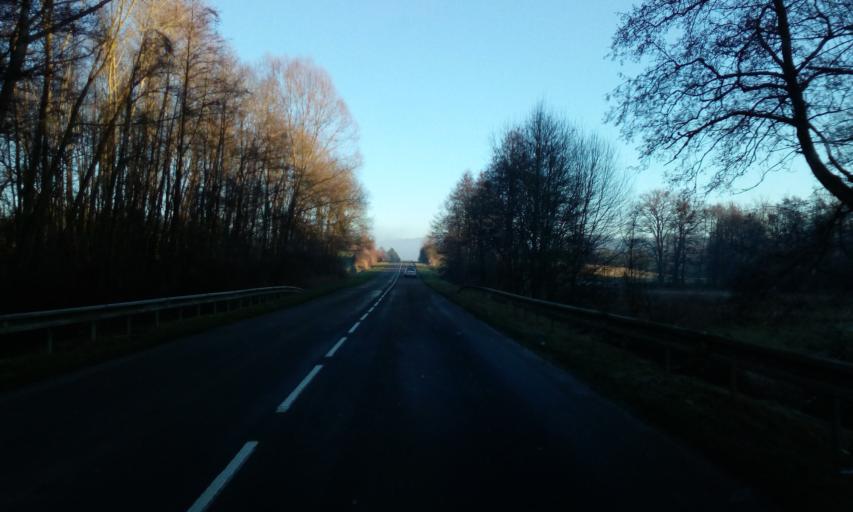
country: FR
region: Champagne-Ardenne
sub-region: Departement des Ardennes
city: Rimogne
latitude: 49.7769
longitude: 4.4140
